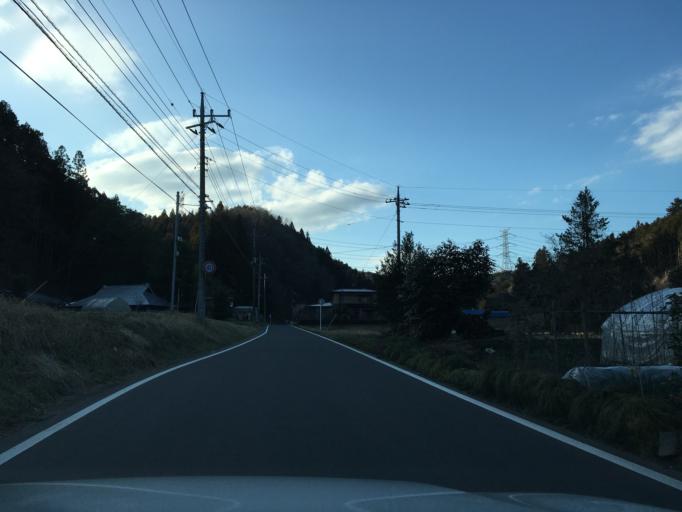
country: JP
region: Tochigi
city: Otawara
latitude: 36.8399
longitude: 140.1902
